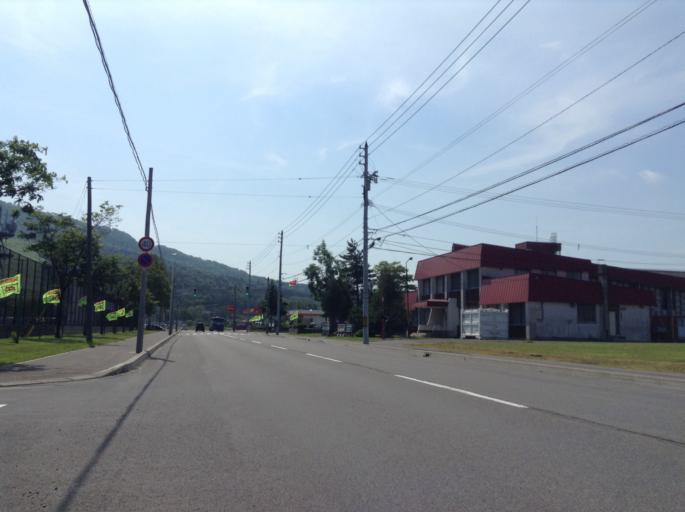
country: JP
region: Hokkaido
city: Nayoro
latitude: 44.7262
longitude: 142.2619
